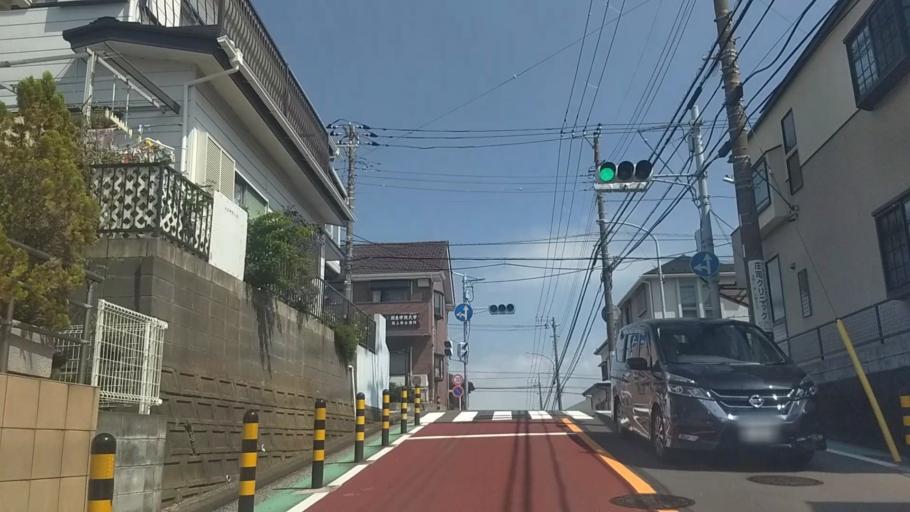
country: JP
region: Kanagawa
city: Zushi
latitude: 35.3327
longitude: 139.6038
